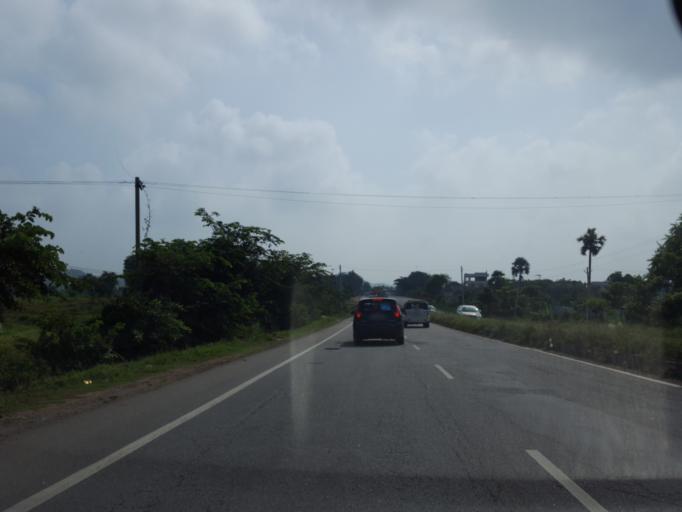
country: IN
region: Telangana
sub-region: Rangareddi
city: Ghatkesar
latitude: 17.2921
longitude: 78.7570
